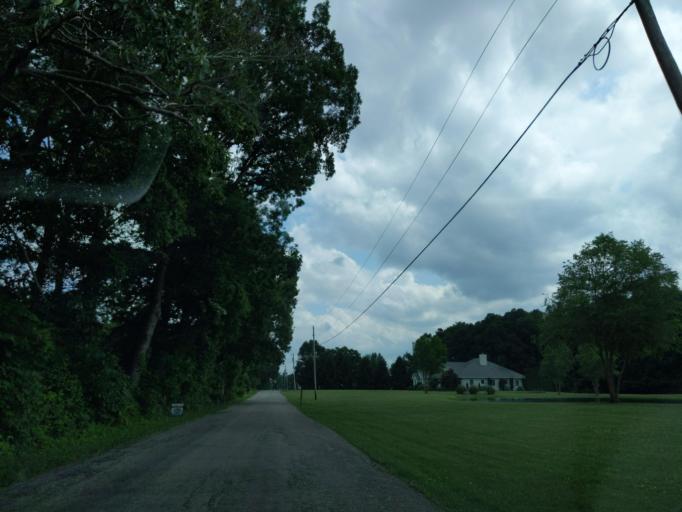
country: US
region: Indiana
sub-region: Ripley County
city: Batesville
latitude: 39.3259
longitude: -85.1899
